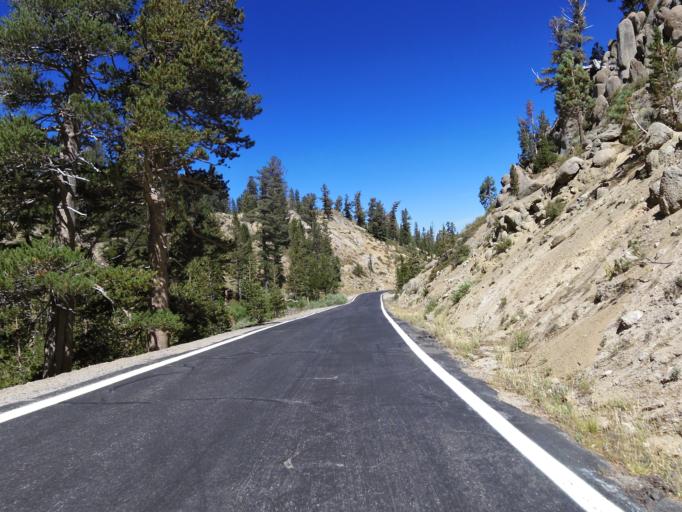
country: US
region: Nevada
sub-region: Douglas County
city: Gardnerville Ranchos
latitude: 38.5579
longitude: -119.8081
